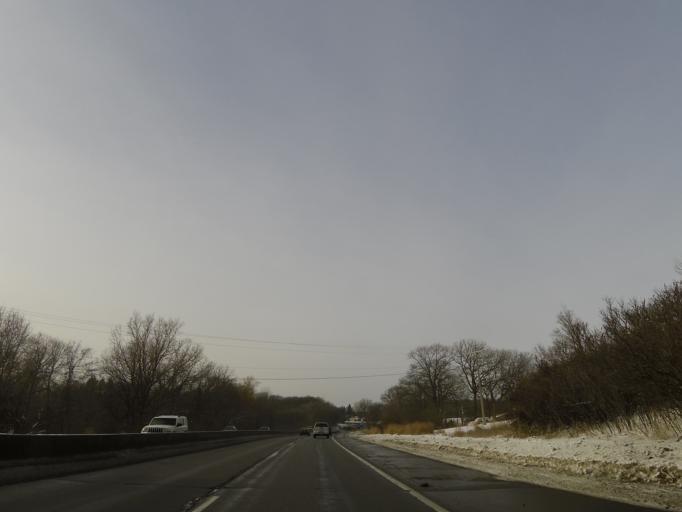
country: US
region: Minnesota
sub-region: Hennepin County
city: Deephaven
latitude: 44.9063
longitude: -93.5382
